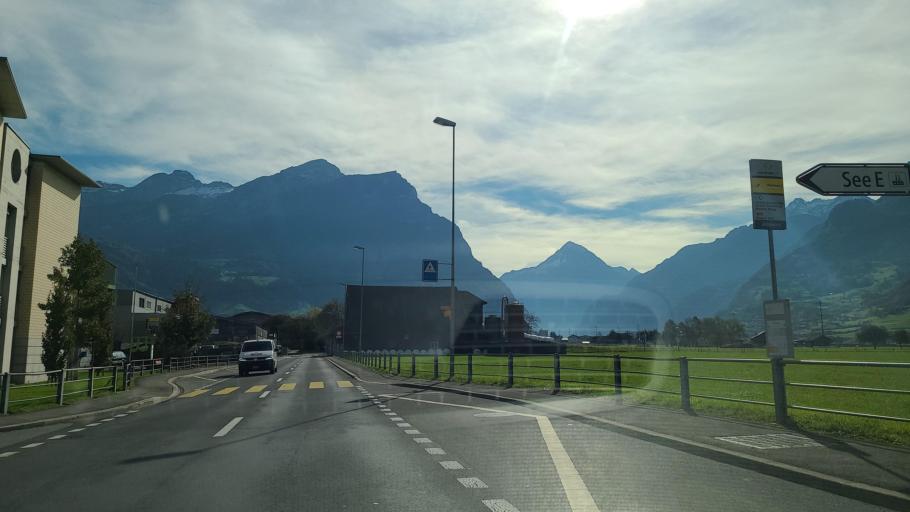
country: CH
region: Uri
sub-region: Uri
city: Seedorf
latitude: 46.8833
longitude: 8.6273
